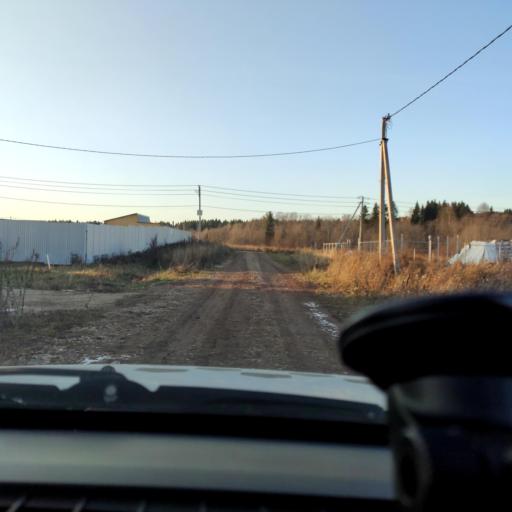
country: RU
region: Perm
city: Ferma
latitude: 57.9481
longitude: 56.3478
